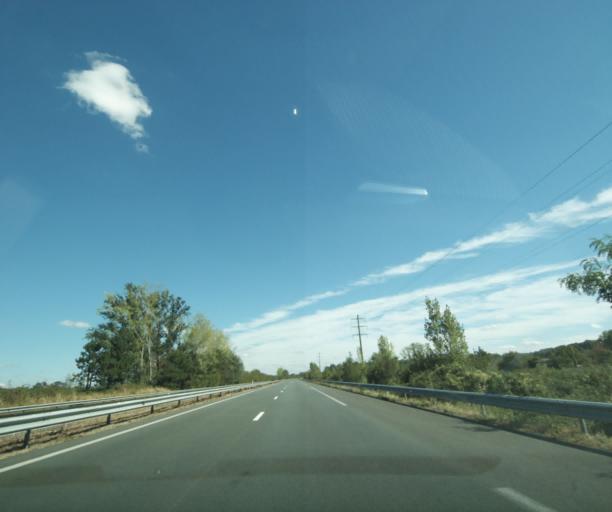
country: FR
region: Aquitaine
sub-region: Departement du Lot-et-Garonne
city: Sainte-Colombe-en-Bruilhois
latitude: 44.2117
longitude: 0.4606
